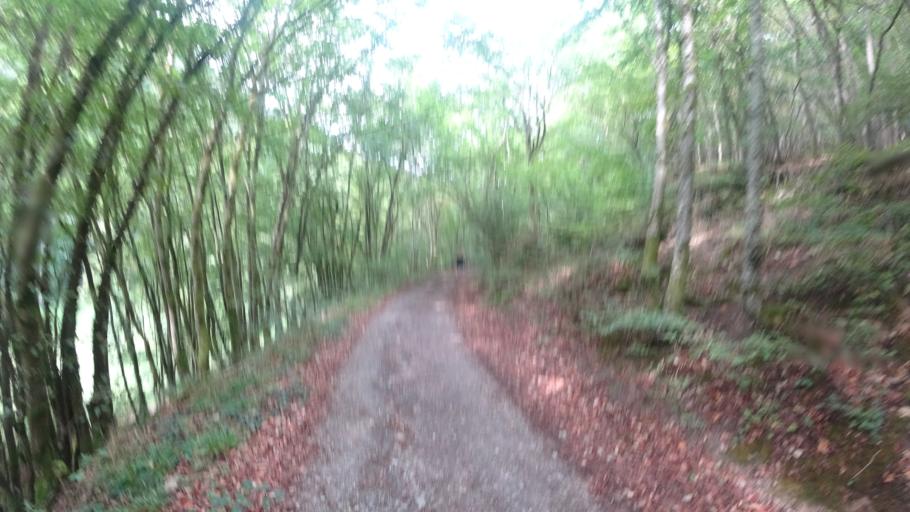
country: DE
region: Rheinland-Pfalz
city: Beulich
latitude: 50.1980
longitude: 7.4619
